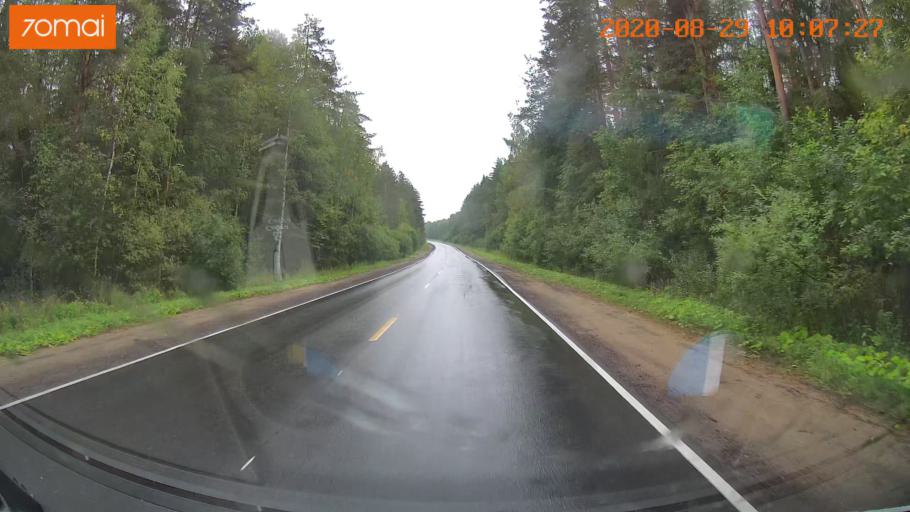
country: RU
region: Ivanovo
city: Kuznechikha
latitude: 57.3807
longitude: 42.5673
